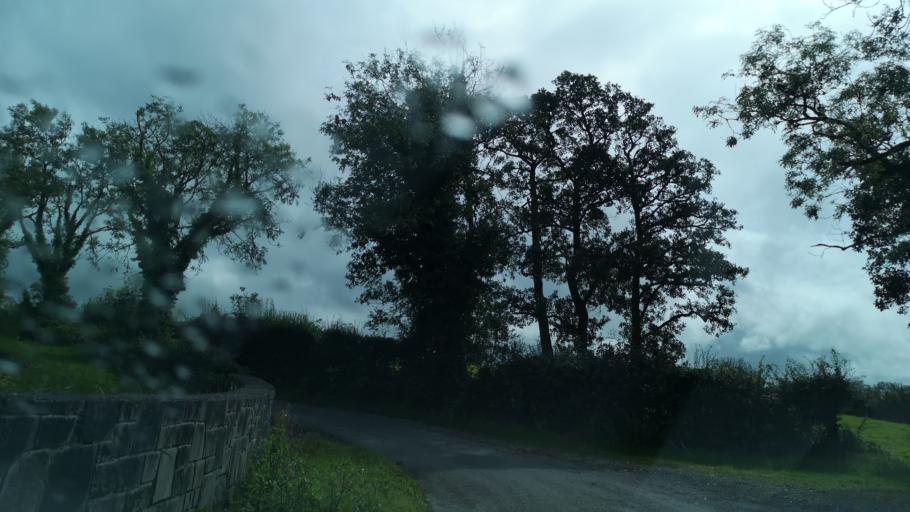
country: IE
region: Connaught
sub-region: County Galway
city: Loughrea
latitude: 53.3040
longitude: -8.5963
